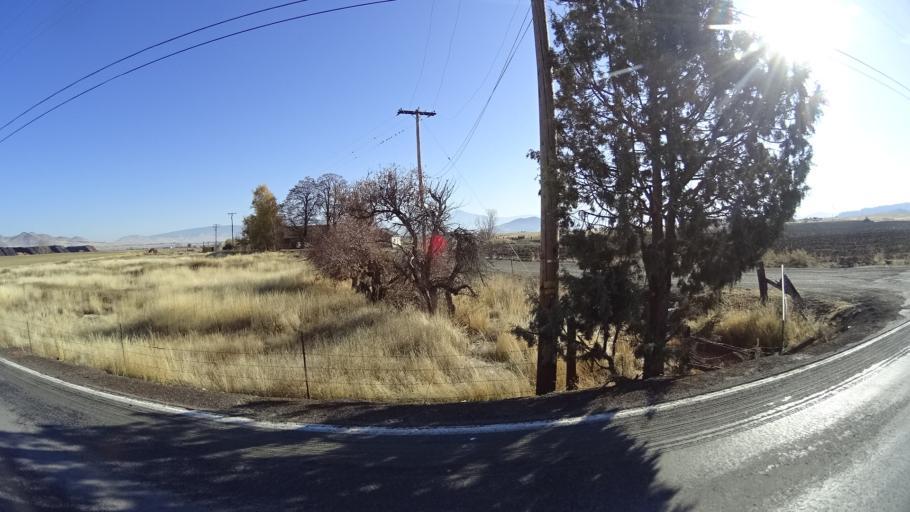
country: US
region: California
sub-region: Siskiyou County
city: Yreka
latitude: 41.7253
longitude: -122.5933
